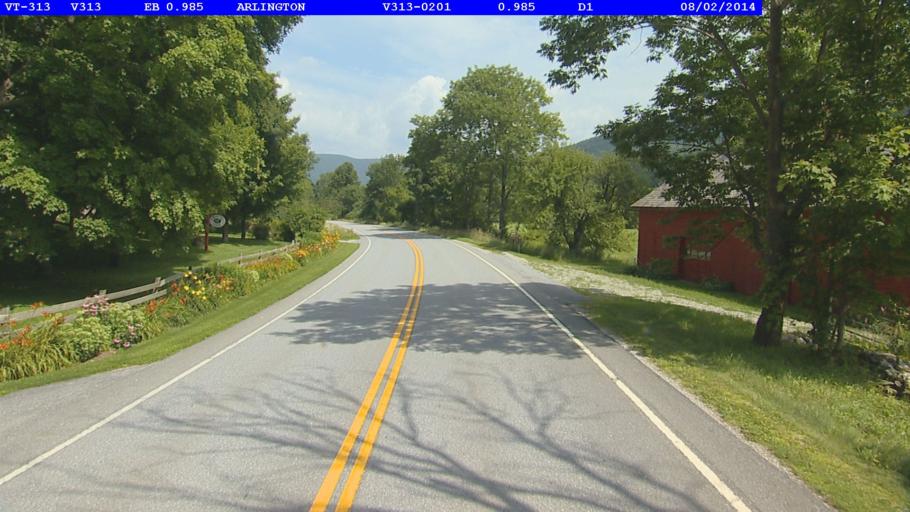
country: US
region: Vermont
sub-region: Bennington County
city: Arlington
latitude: 43.1023
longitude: -73.2471
